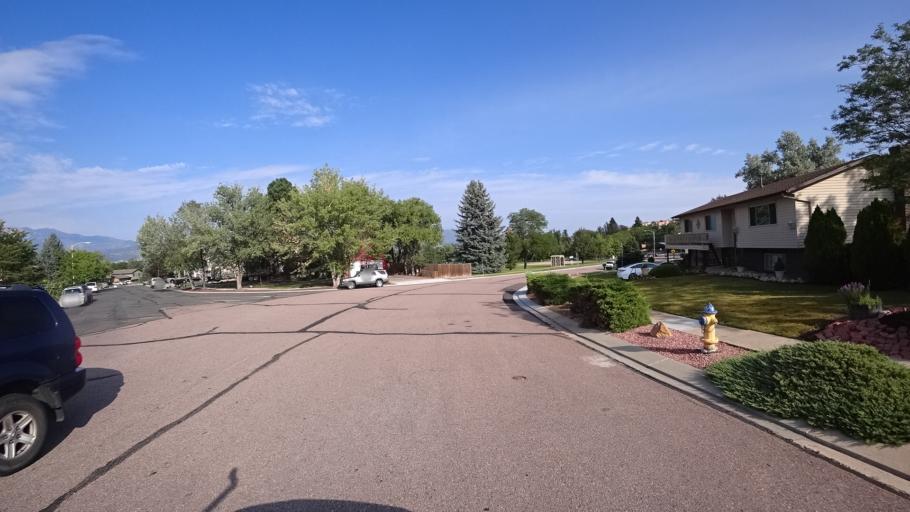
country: US
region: Colorado
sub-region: El Paso County
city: Colorado Springs
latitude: 38.8880
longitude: -104.8036
